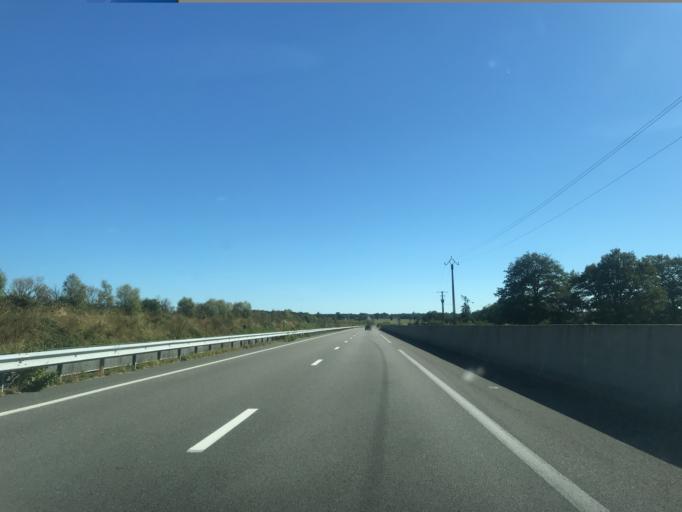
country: FR
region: Limousin
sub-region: Departement de la Creuse
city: Gouzon
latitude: 46.2123
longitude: 2.2792
